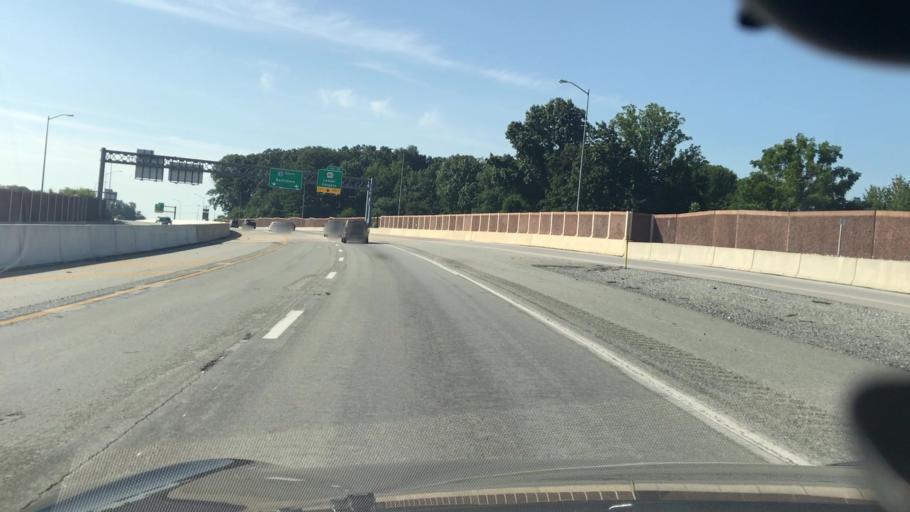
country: US
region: Pennsylvania
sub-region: York County
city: Spry
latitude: 39.9167
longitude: -76.7047
